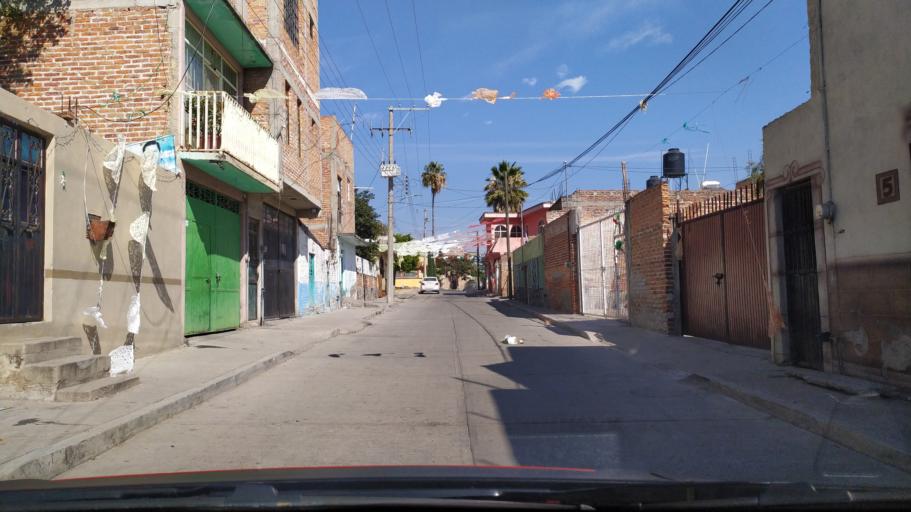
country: MX
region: Guanajuato
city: Ciudad Manuel Doblado
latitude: 20.7323
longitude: -101.9549
